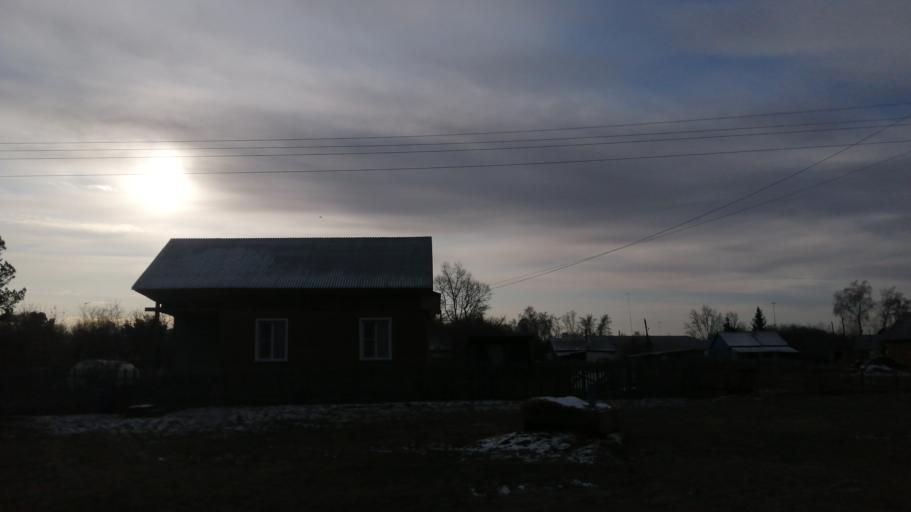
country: RU
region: Novosibirsk
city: Krasnozerskoye
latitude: 53.9876
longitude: 78.7165
